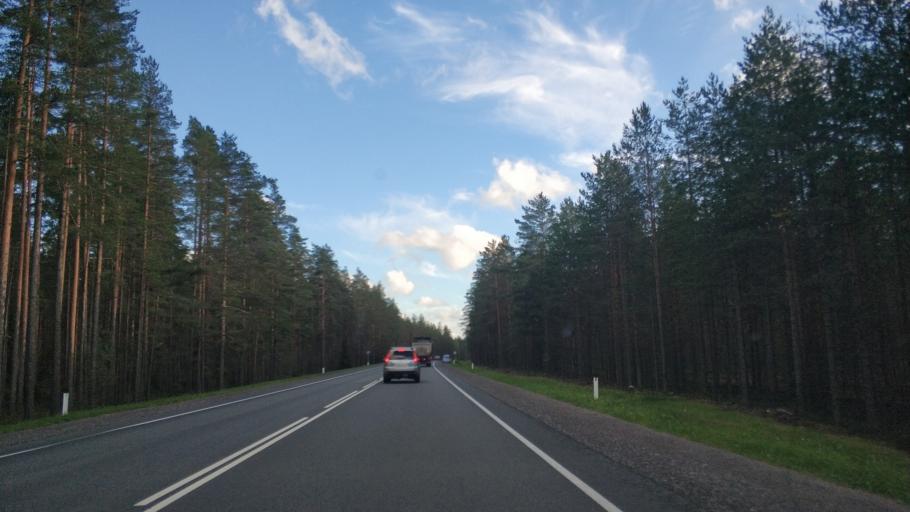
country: RU
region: Leningrad
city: Priozersk
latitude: 60.8877
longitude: 30.1603
